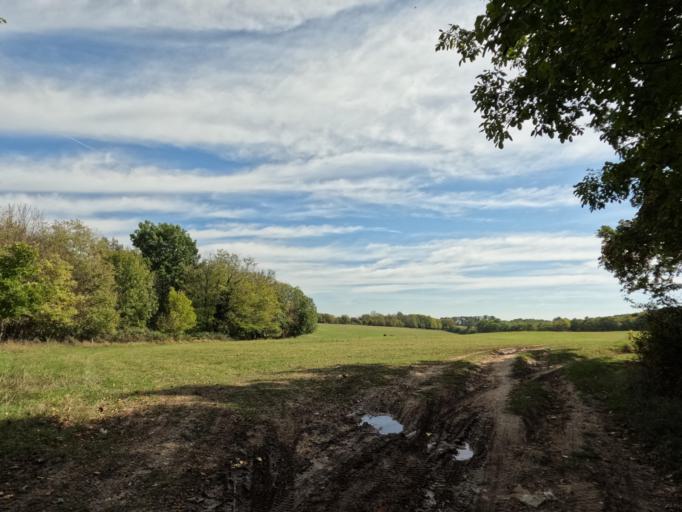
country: HU
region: Tolna
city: Szentgalpuszta
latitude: 46.3305
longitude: 18.6478
